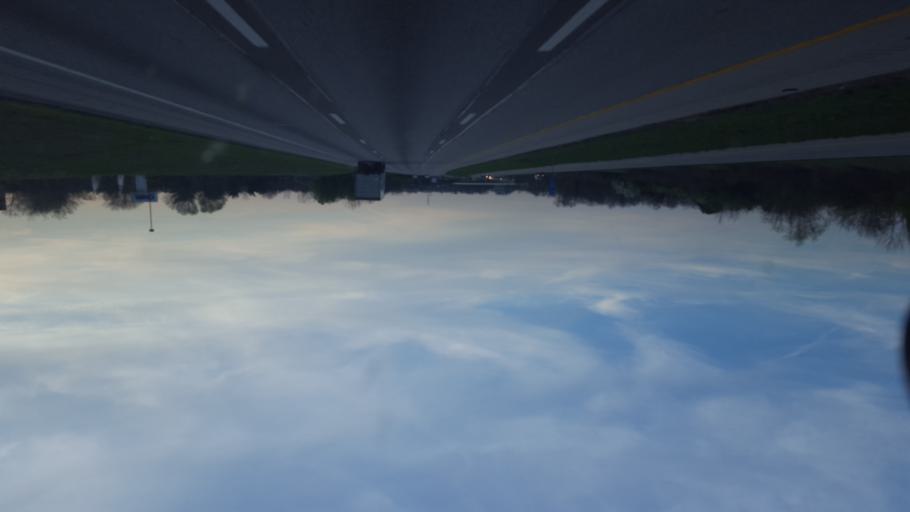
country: US
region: Ohio
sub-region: Warren County
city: Landen
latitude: 39.3415
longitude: -84.2793
